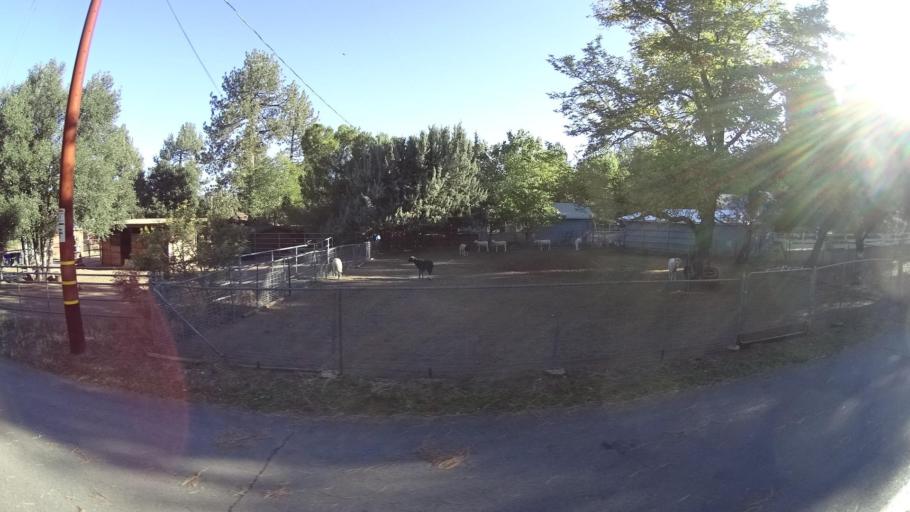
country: US
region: California
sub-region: San Diego County
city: Pine Valley
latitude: 32.8195
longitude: -116.5284
